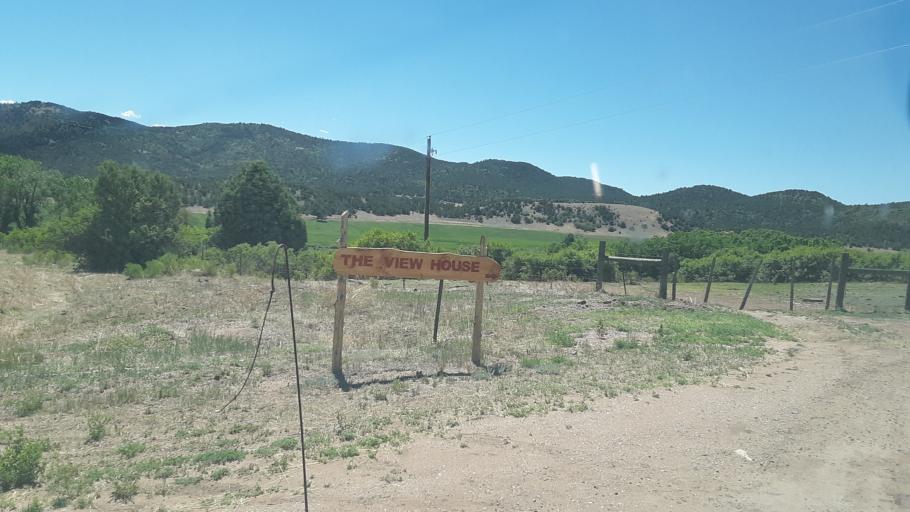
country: US
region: Colorado
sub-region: Custer County
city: Westcliffe
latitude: 38.2835
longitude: -105.6061
